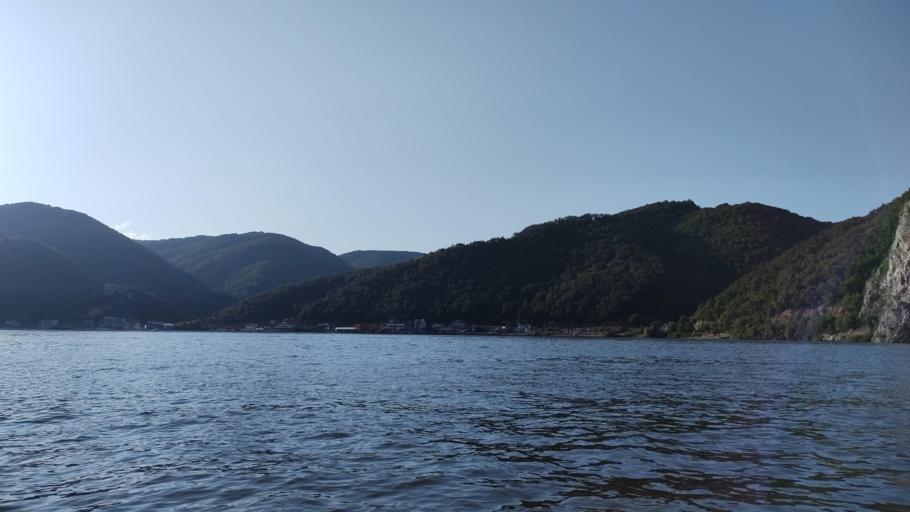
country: RO
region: Mehedinti
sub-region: Comuna Dubova
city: Dubova
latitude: 44.6270
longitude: 22.2791
